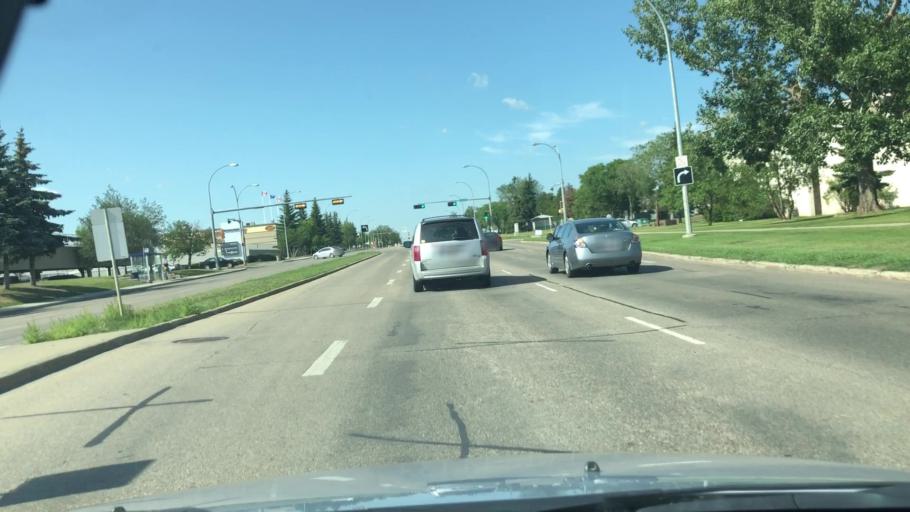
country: CA
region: Alberta
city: Edmonton
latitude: 53.6009
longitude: -113.4429
